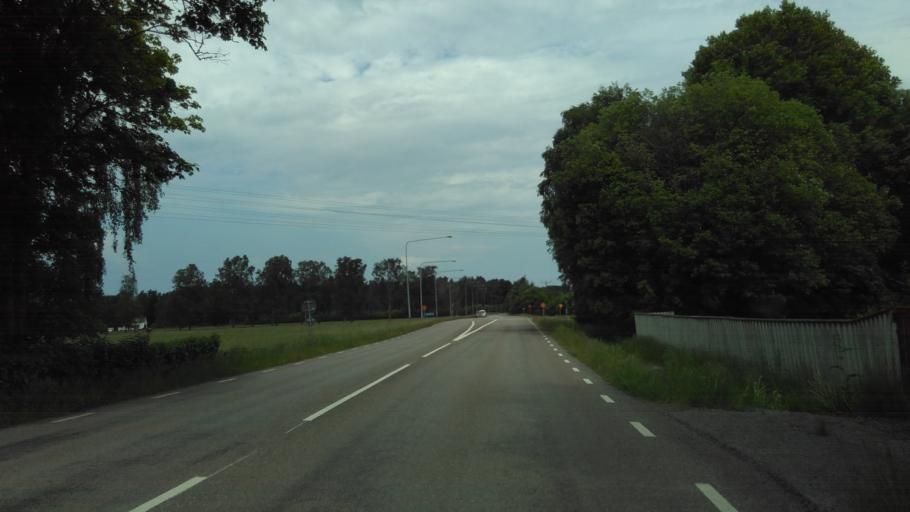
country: SE
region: Vaestra Goetaland
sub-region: Lidkopings Kommun
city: Lidkoping
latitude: 58.4799
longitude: 13.1368
